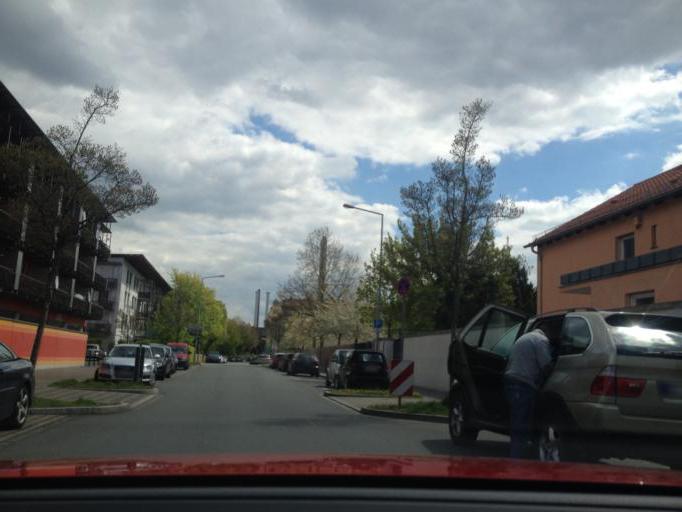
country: DE
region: Bavaria
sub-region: Regierungsbezirk Mittelfranken
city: Grossreuth bei Schweinau
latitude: 49.4415
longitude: 11.0508
